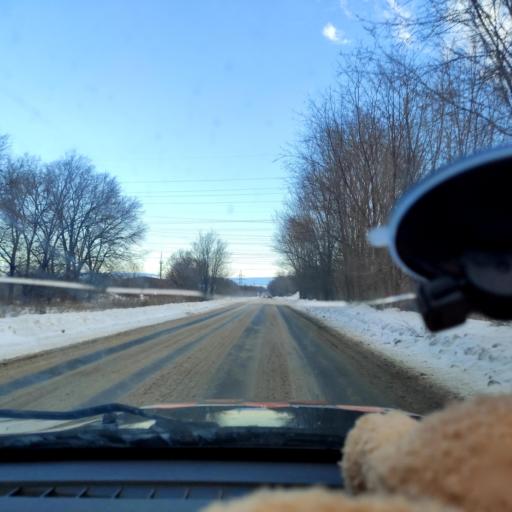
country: RU
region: Samara
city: Tol'yatti
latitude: 53.5762
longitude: 49.2550
